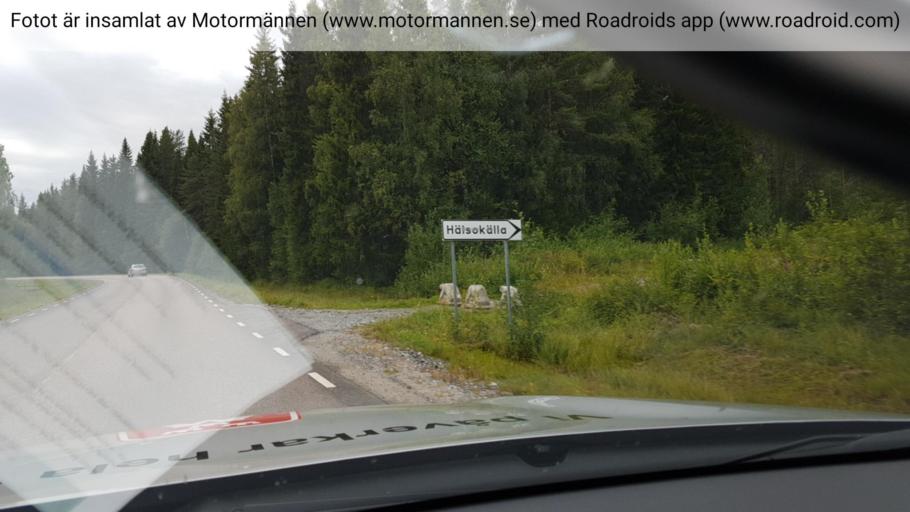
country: SE
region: Norrbotten
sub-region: Lulea Kommun
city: Gammelstad
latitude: 65.6571
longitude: 22.0436
